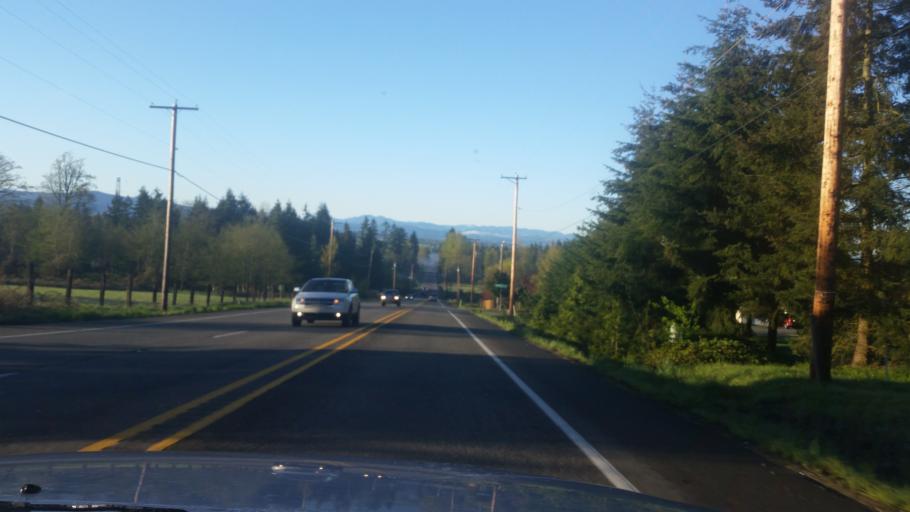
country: US
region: Washington
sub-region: Pierce County
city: Graham
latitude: 47.0241
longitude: -122.2963
